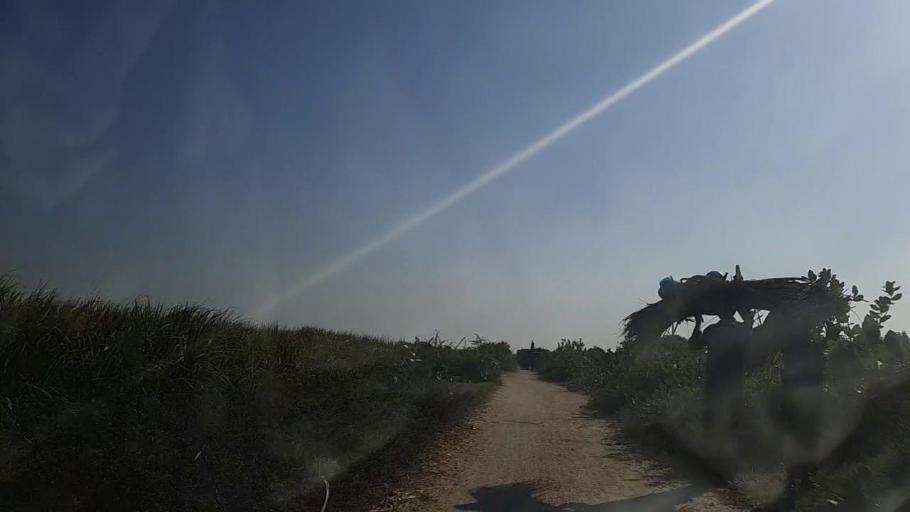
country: PK
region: Sindh
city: Mirpur Batoro
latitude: 24.6381
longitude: 68.1623
